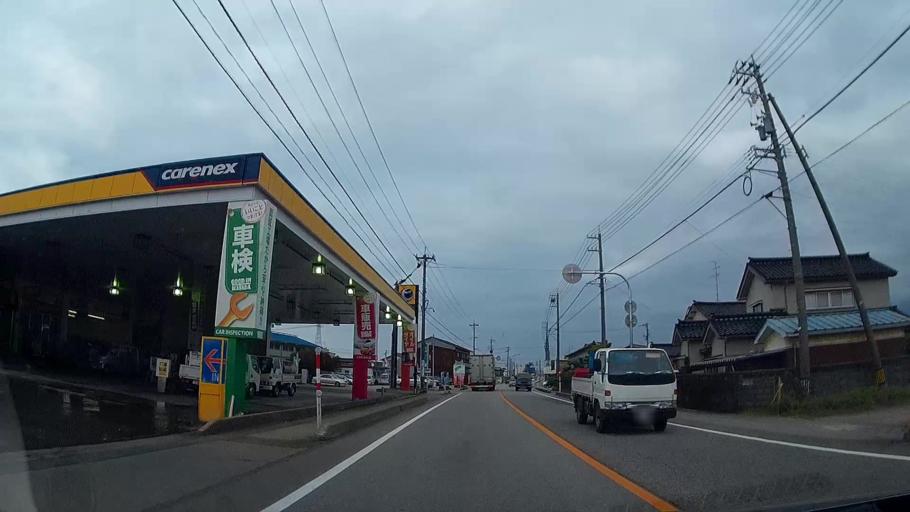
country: JP
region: Toyama
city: Nyuzen
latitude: 36.9359
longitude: 137.5065
